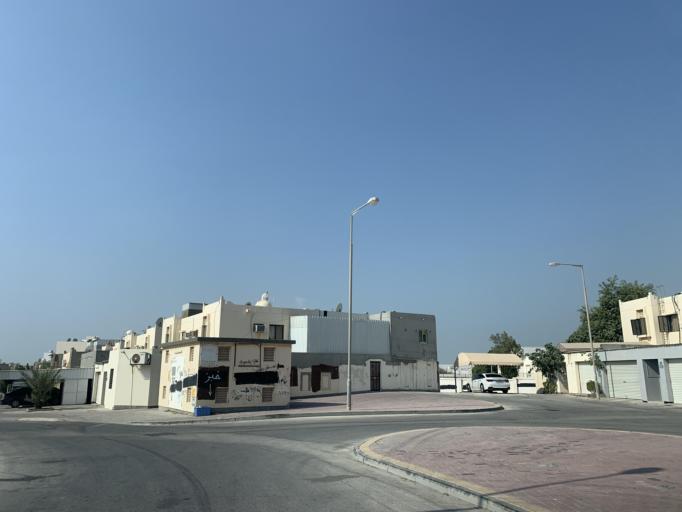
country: BH
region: Central Governorate
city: Madinat Hamad
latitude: 26.1107
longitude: 50.5013
